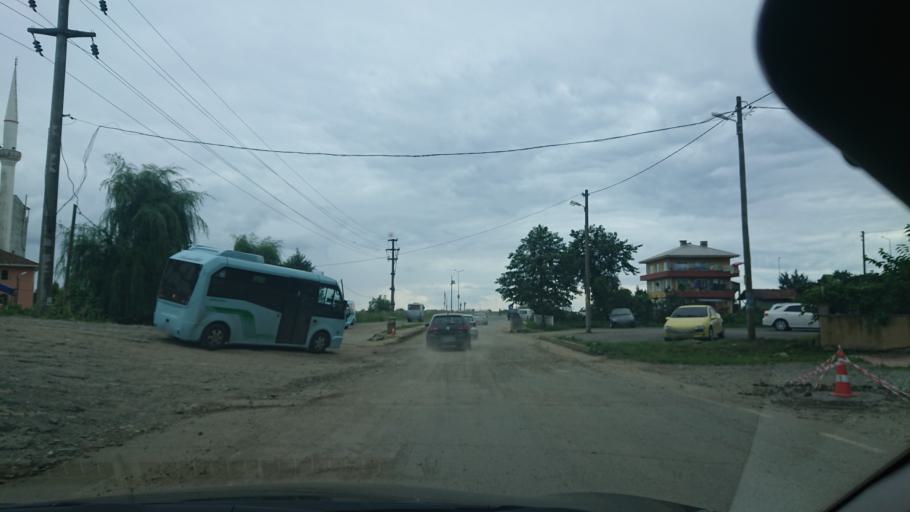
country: TR
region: Rize
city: Rize
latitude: 41.0339
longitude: 40.4807
